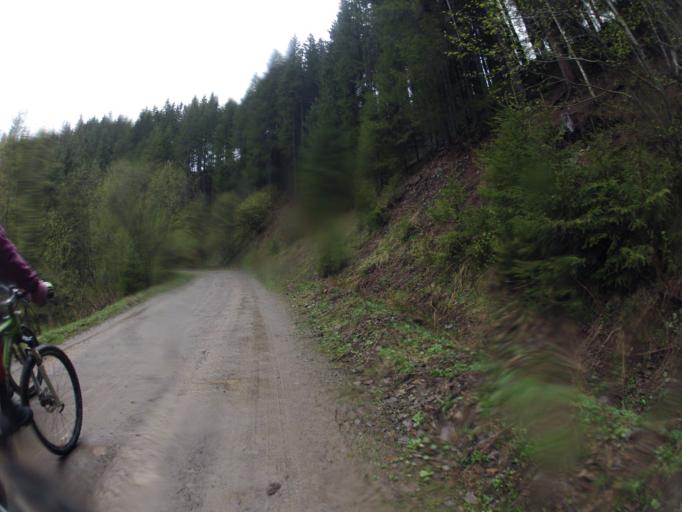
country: RO
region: Suceava
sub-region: Comuna Izvoarele Sucevei
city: Izvoarele Sucevei
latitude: 47.8347
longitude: 25.0477
